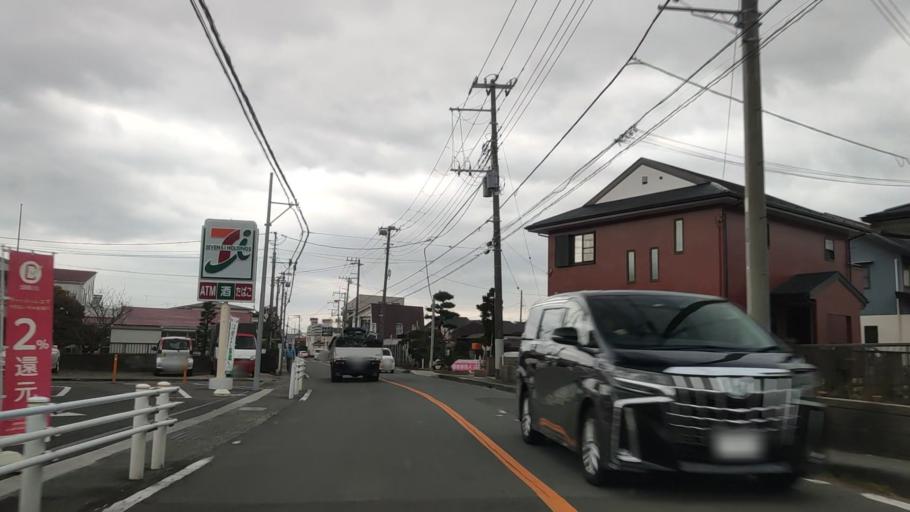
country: JP
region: Kanagawa
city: Odawara
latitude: 35.2827
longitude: 139.1990
